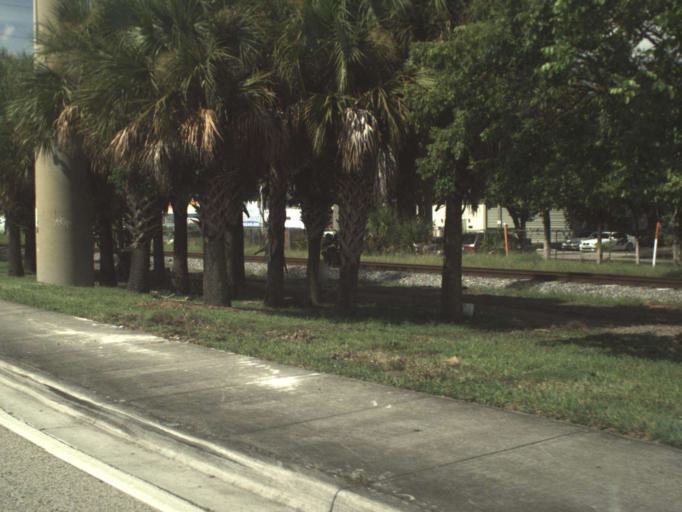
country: US
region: Florida
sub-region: Miami-Dade County
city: North Miami Beach
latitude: 25.9279
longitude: -80.1534
